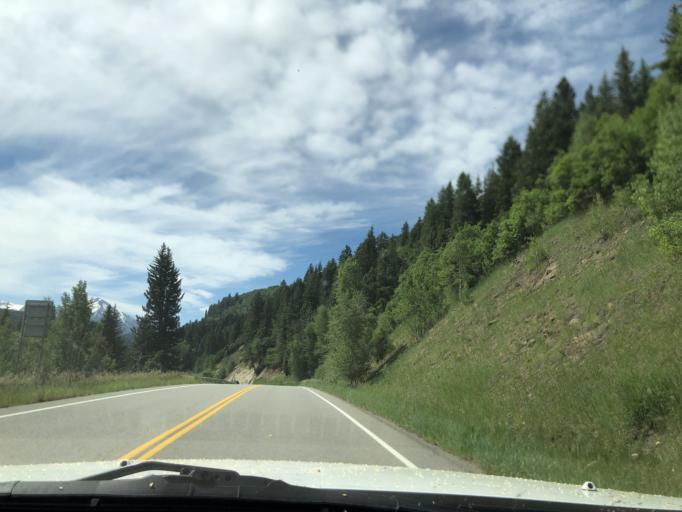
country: US
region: Colorado
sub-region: Delta County
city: Paonia
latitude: 38.9860
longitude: -107.3482
